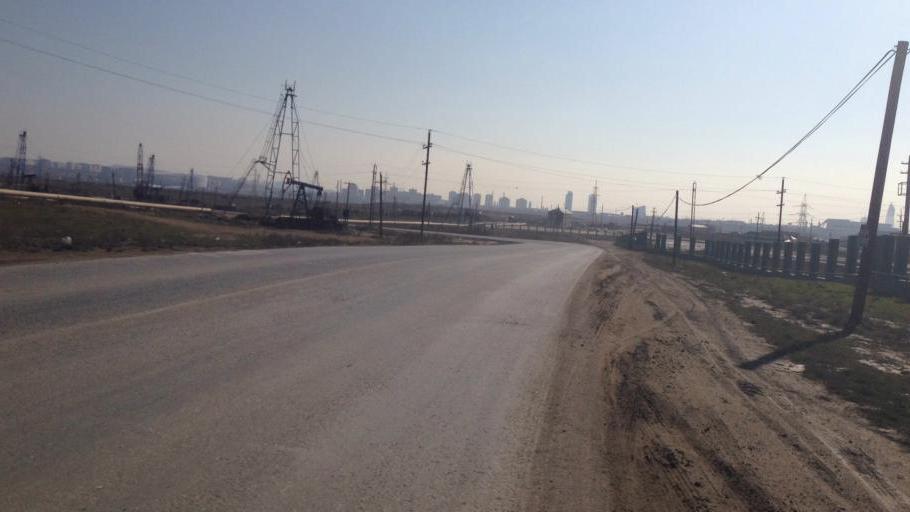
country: AZ
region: Baki
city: Balakhani
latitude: 40.4583
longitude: 49.8913
